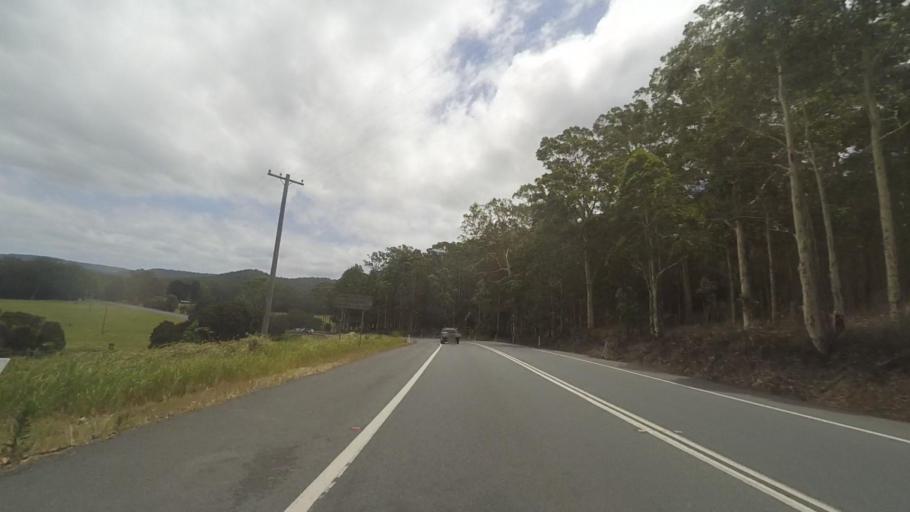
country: AU
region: New South Wales
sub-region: Shoalhaven Shire
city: Falls Creek
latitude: -35.0812
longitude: 150.5268
